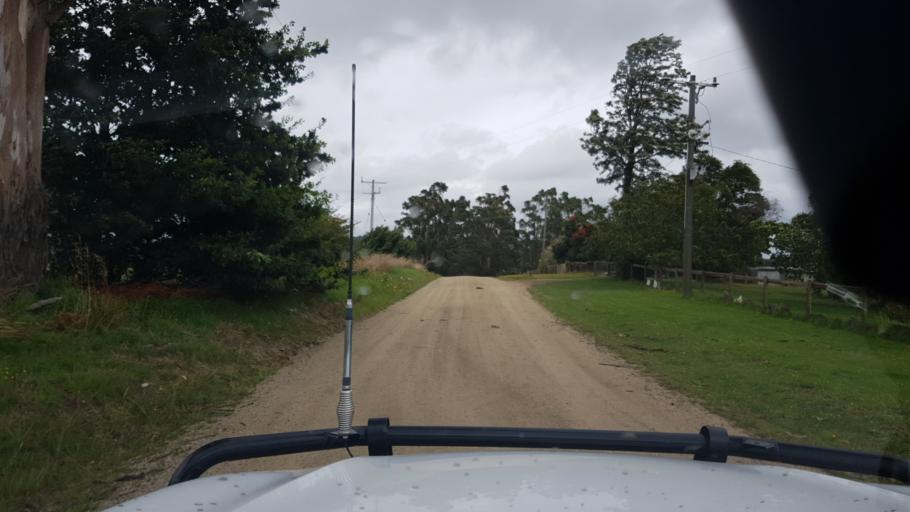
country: AU
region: Victoria
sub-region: Baw Baw
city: Warragul
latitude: -38.1860
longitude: 145.8663
